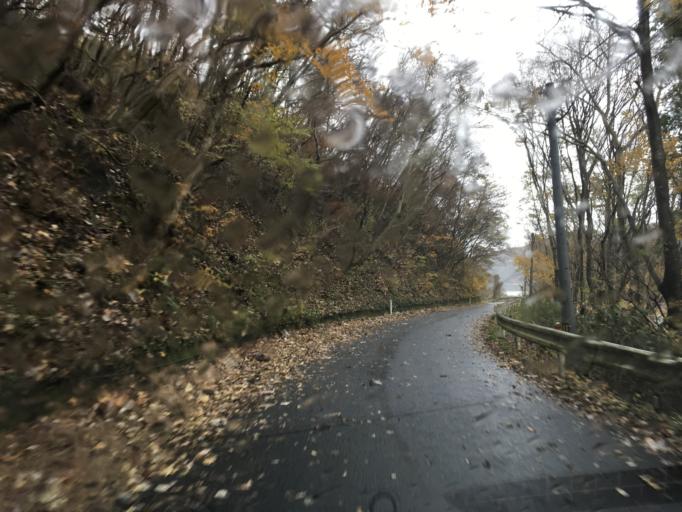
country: JP
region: Iwate
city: Ichinoseki
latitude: 38.8129
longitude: 141.2525
